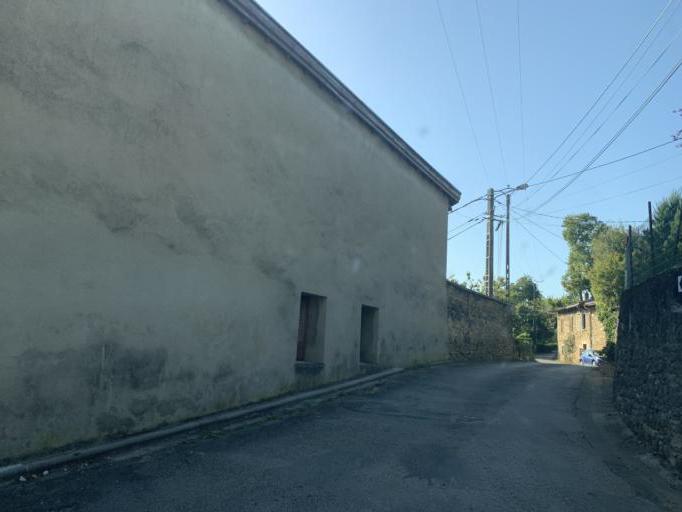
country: FR
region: Rhone-Alpes
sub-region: Departement de l'Ain
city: Vaux-en-Bugey
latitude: 45.9487
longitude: 5.3709
